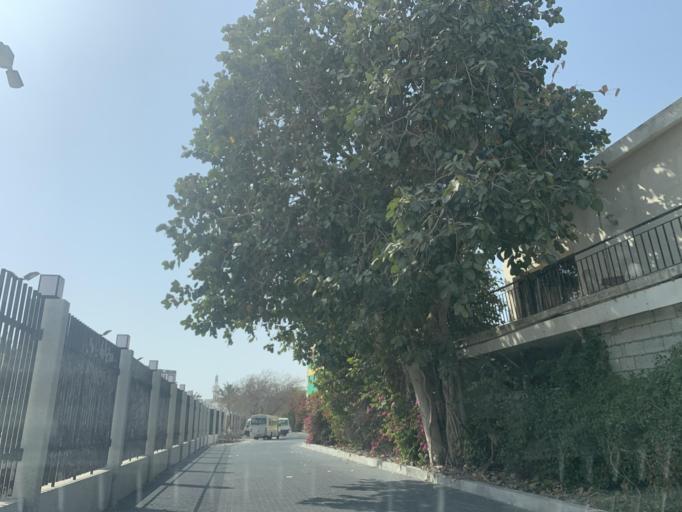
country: BH
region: Manama
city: Manama
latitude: 26.2225
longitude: 50.5671
